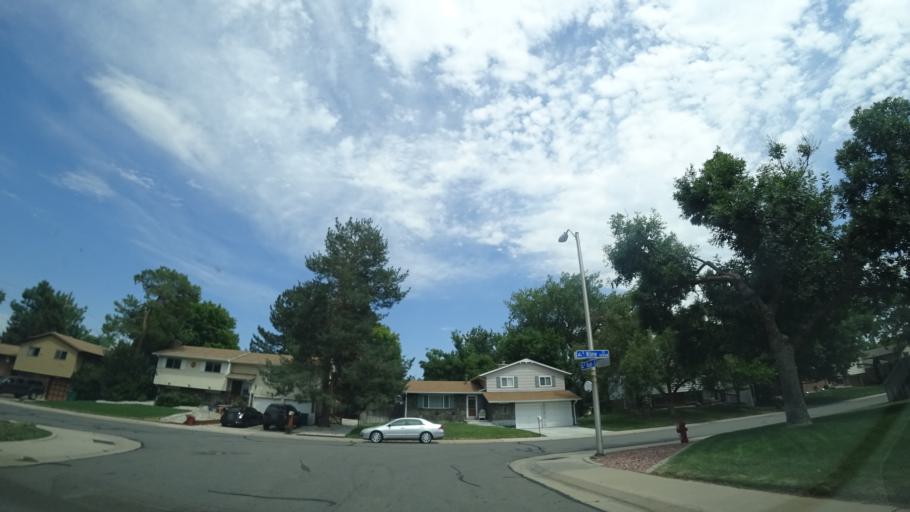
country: US
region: Colorado
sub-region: Jefferson County
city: Lakewood
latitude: 39.6960
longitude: -105.1110
